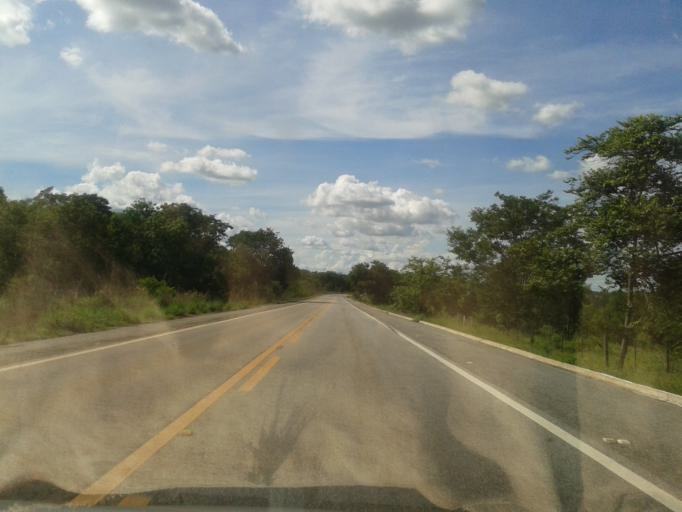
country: BR
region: Goias
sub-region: Mozarlandia
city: Mozarlandia
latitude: -15.1255
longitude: -50.6008
